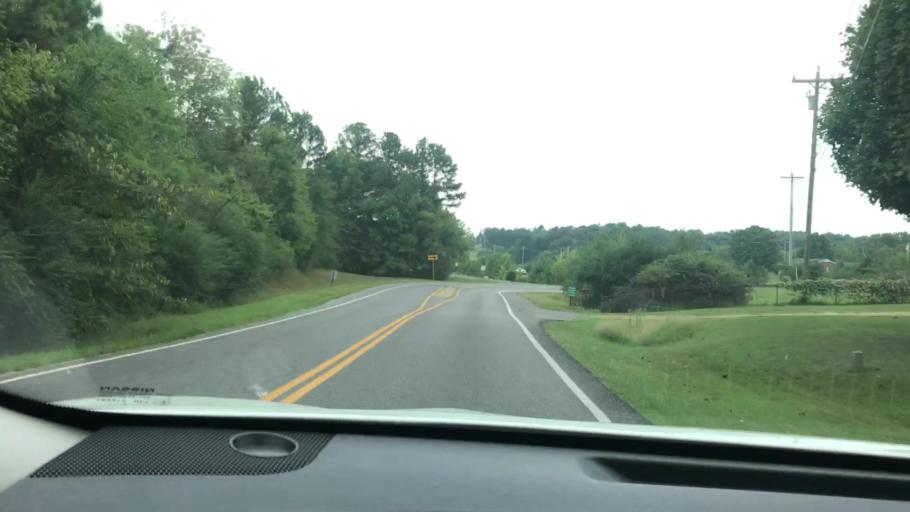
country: US
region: Kentucky
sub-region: Calloway County
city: Murray
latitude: 36.6777
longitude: -88.3014
